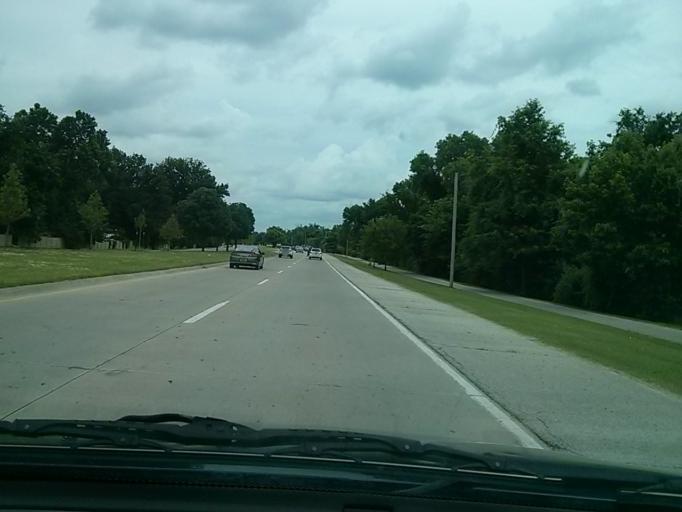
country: US
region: Oklahoma
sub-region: Tulsa County
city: Jenks
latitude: 36.0350
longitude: -95.9572
